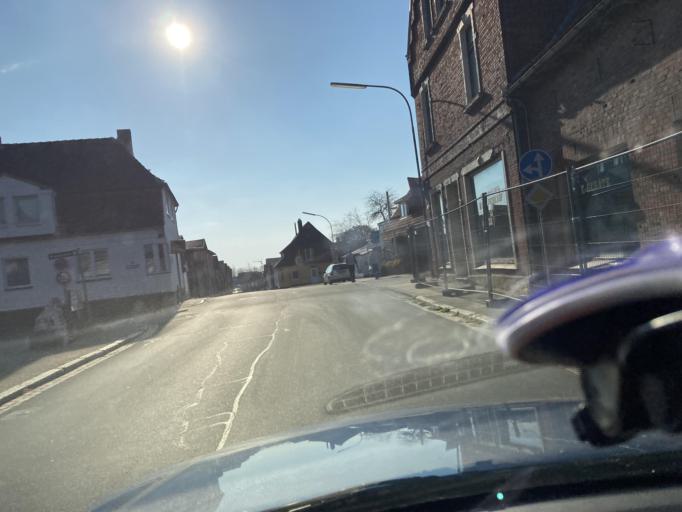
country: DE
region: Schleswig-Holstein
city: Meldorf
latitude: 54.0871
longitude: 9.0722
